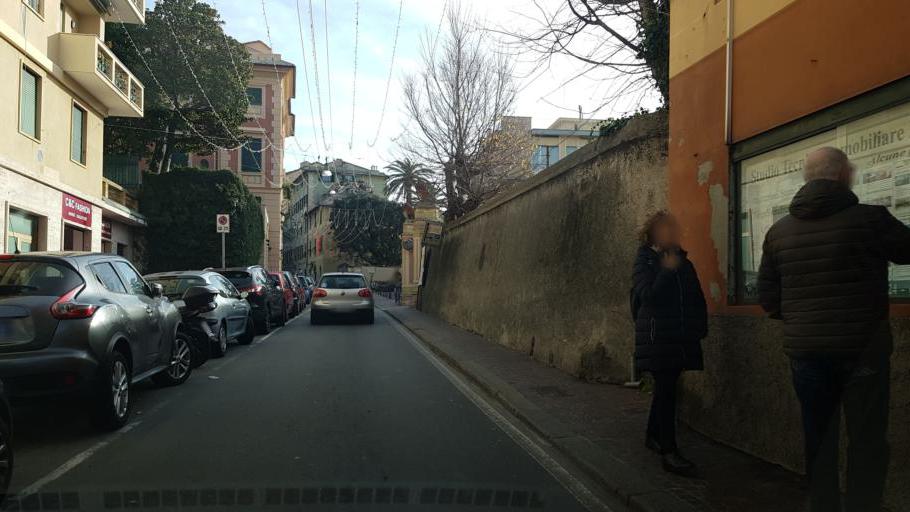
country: IT
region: Liguria
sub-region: Provincia di Genova
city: Bogliasco
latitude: 44.3840
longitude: 9.0368
